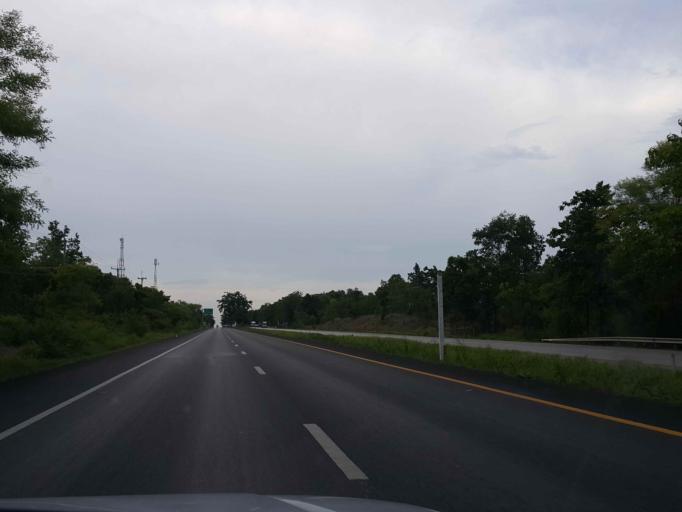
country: TH
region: Lampang
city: Ko Kha
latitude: 18.0881
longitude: 99.3958
